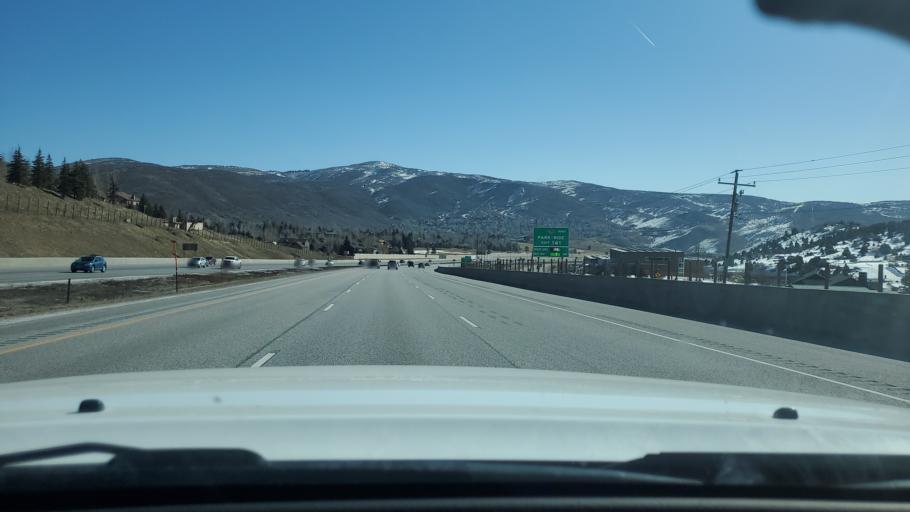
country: US
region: Utah
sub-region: Summit County
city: Summit Park
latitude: 40.7534
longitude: -111.5899
